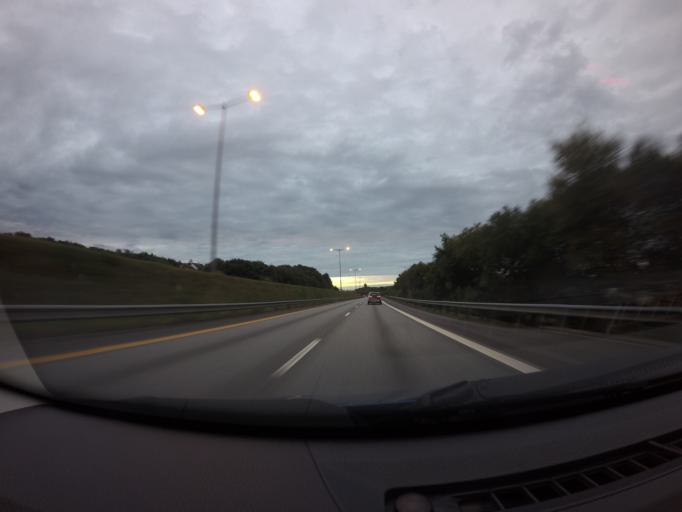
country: NO
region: Rogaland
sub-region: Sandnes
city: Sandnes
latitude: 58.8982
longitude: 5.7095
